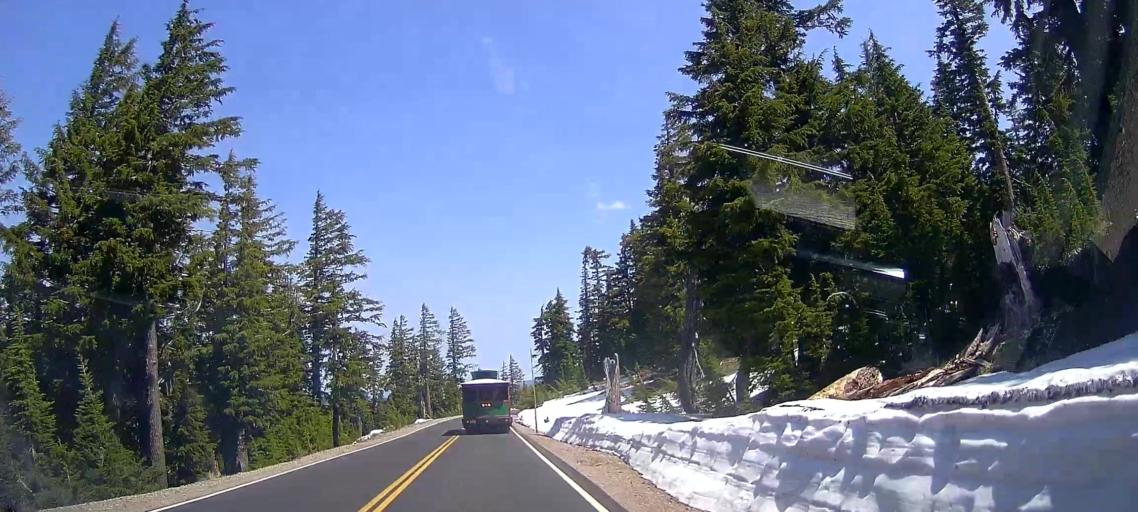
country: US
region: Oregon
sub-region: Jackson County
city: Shady Cove
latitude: 42.9768
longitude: -122.1431
